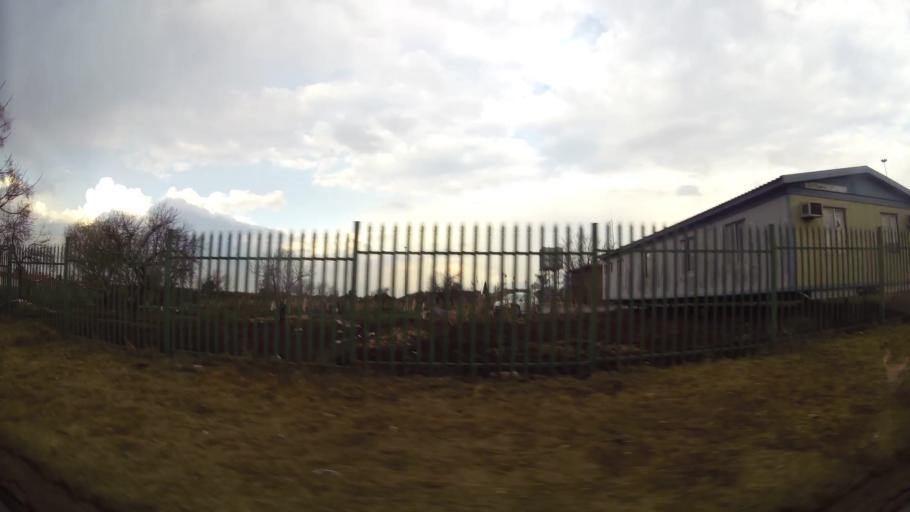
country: ZA
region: Gauteng
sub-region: Ekurhuleni Metropolitan Municipality
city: Germiston
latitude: -26.3699
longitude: 28.1326
